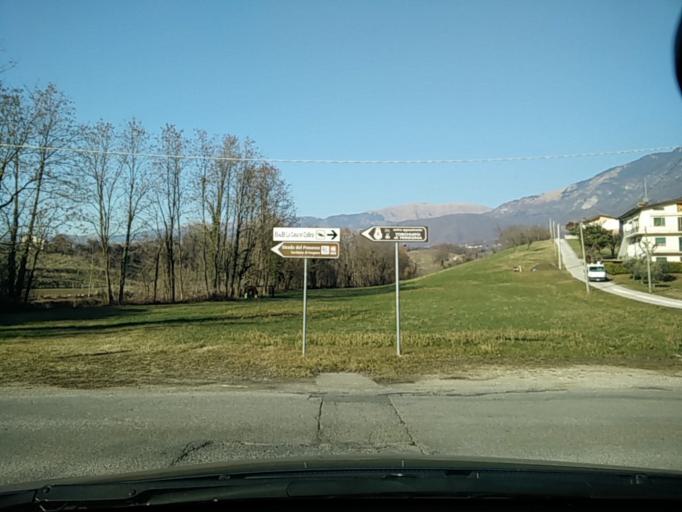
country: IT
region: Veneto
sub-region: Provincia di Treviso
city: Cappella Maggiore
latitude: 45.9901
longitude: 12.3680
